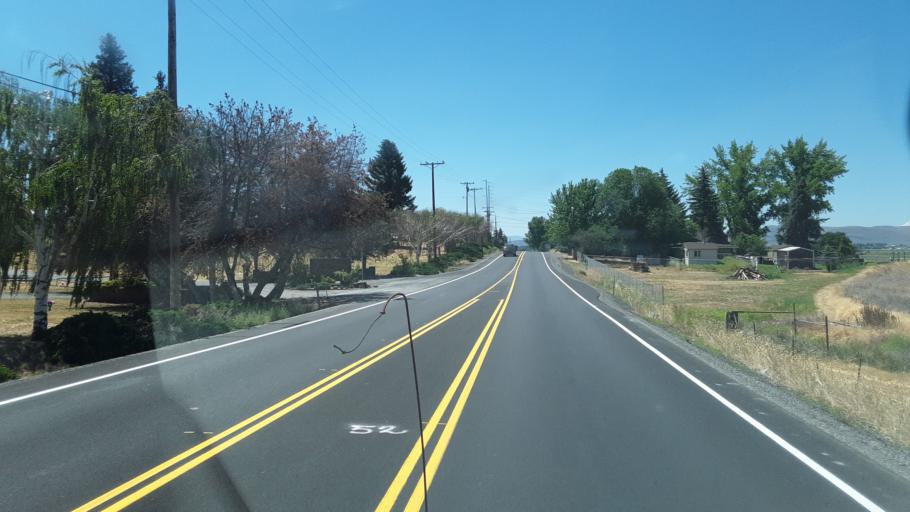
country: US
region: Oregon
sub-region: Klamath County
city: Altamont
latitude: 42.1829
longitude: -121.6982
